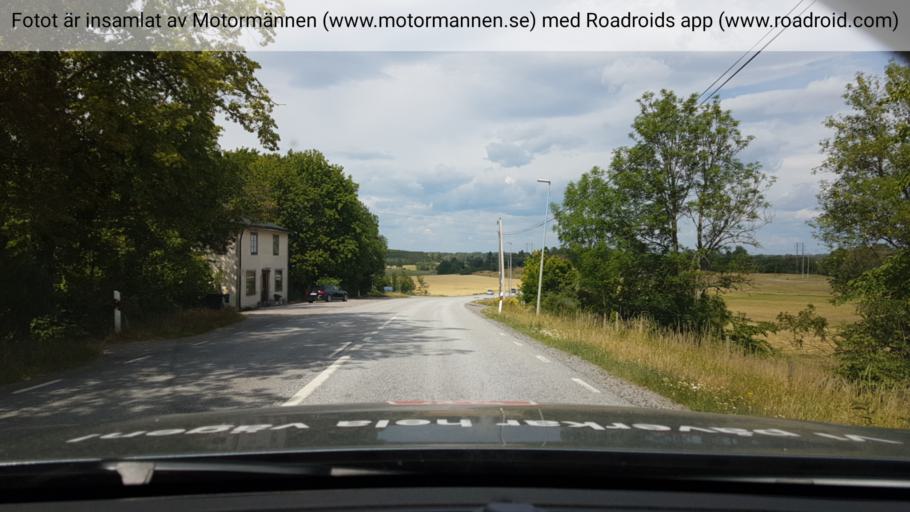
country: SE
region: Uppsala
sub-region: Habo Kommun
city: Balsta
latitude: 59.6114
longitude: 17.6066
